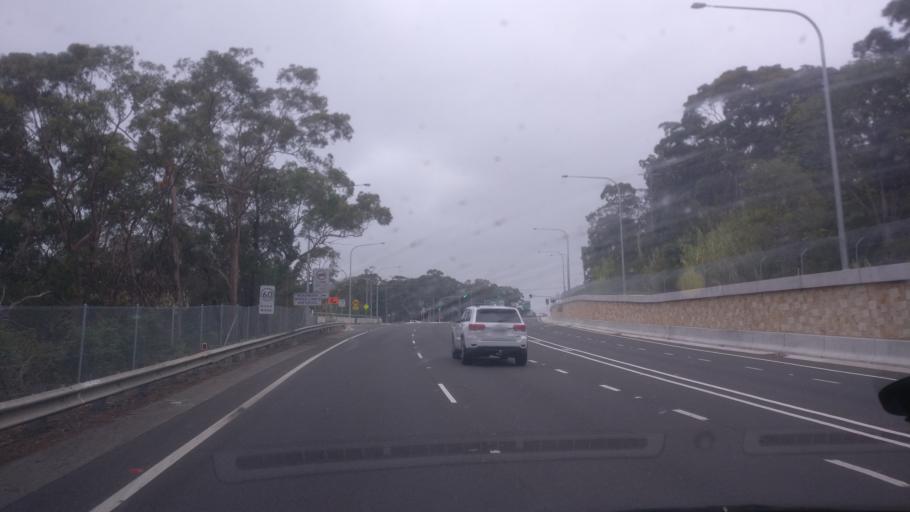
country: AU
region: New South Wales
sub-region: Warringah
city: Allambie Heights
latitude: -33.7482
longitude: 151.2348
